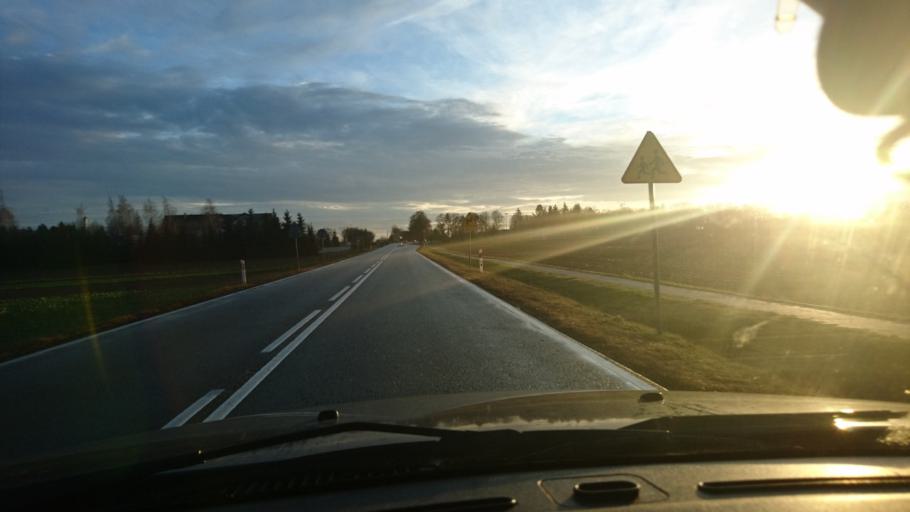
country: PL
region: Greater Poland Voivodeship
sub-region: Powiat kepinski
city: Opatow
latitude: 51.1858
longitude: 18.1468
